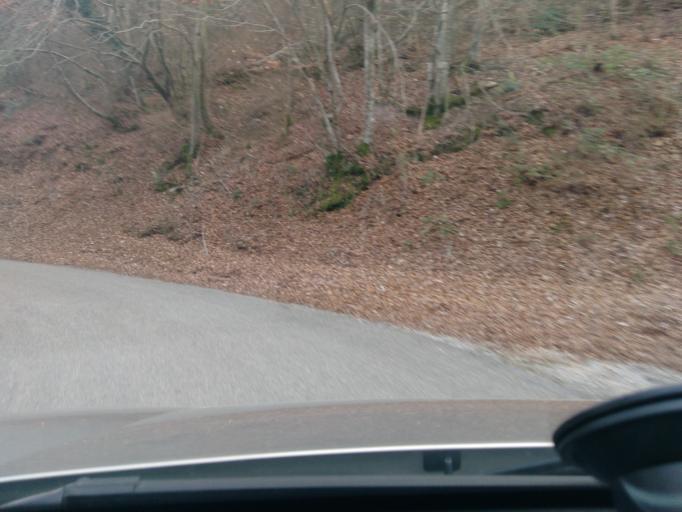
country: FR
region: Rhone-Alpes
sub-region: Departement de l'Ardeche
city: Cruas
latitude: 44.6612
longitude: 4.7386
